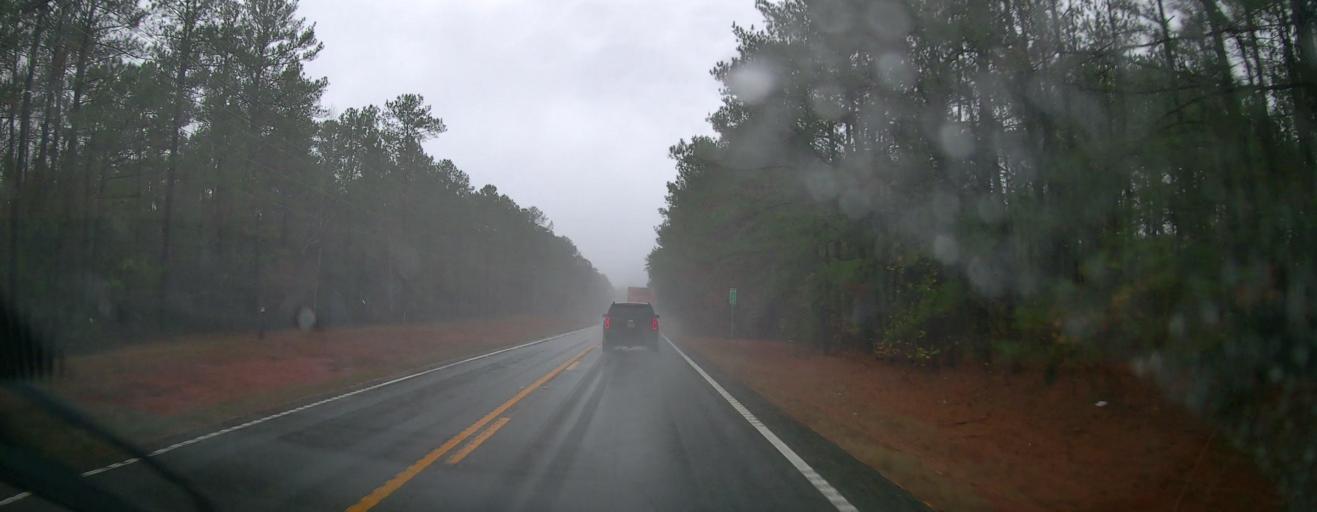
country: US
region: Georgia
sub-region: Putnam County
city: Eatonton
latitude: 33.1777
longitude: -83.4409
